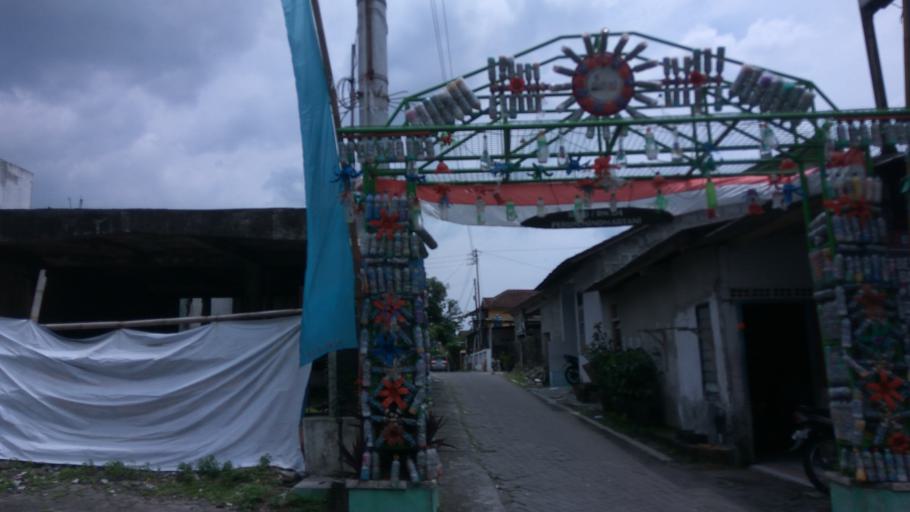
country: ID
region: Daerah Istimewa Yogyakarta
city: Depok
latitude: -7.7433
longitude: 110.4075
